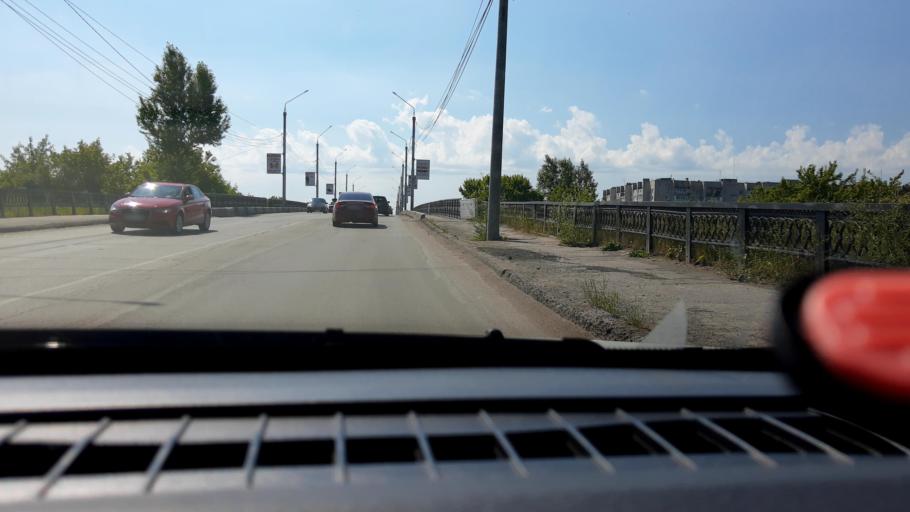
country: RU
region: Nizjnij Novgorod
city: Dzerzhinsk
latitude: 56.2363
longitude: 43.4880
